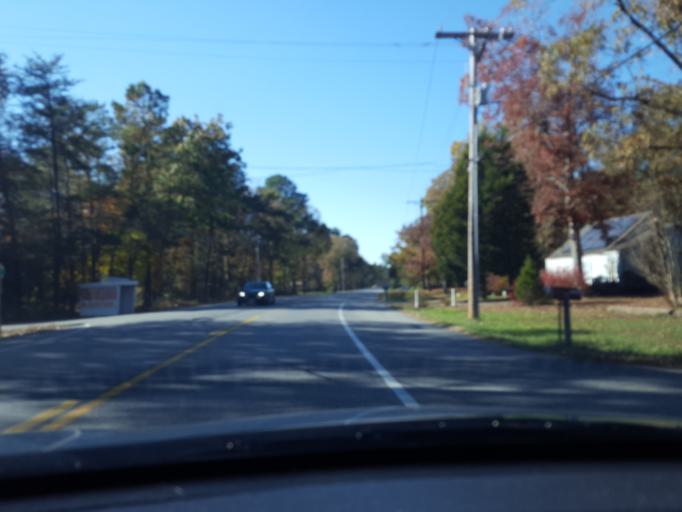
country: US
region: Maryland
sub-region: Saint Mary's County
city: California
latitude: 38.2831
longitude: -76.5620
